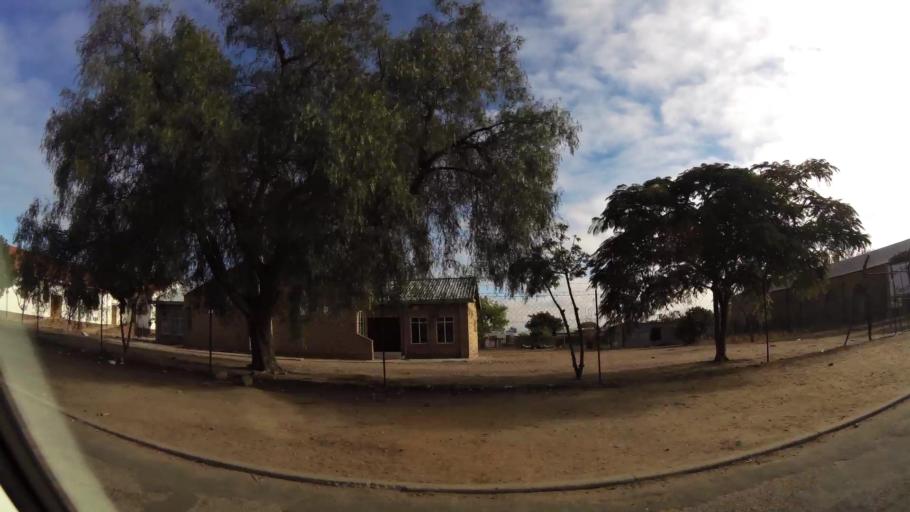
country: ZA
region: Limpopo
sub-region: Capricorn District Municipality
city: Polokwane
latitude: -23.8443
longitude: 29.3848
